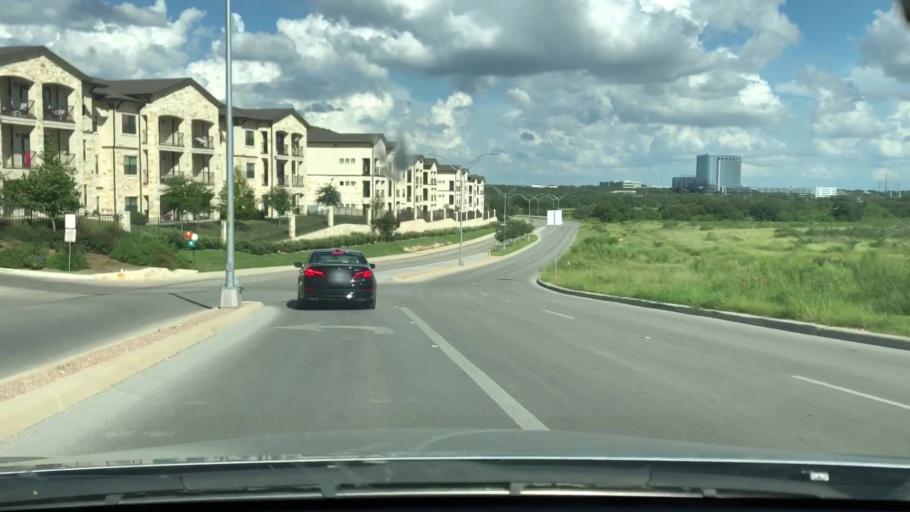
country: US
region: Texas
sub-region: Bexar County
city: Hollywood Park
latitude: 29.6187
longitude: -98.4747
